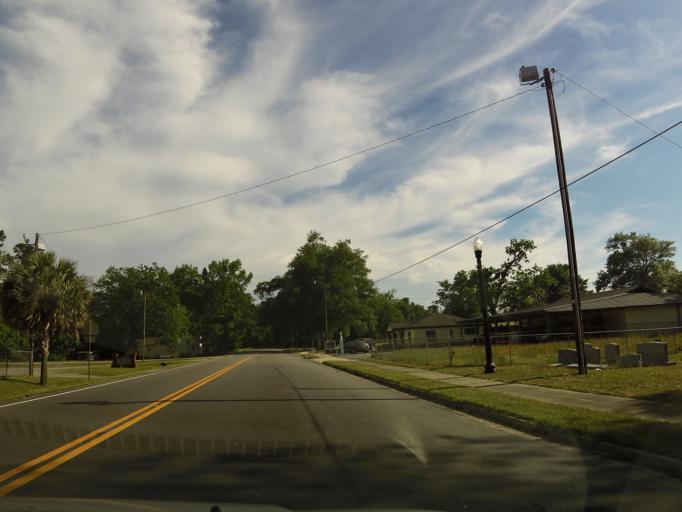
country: US
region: South Carolina
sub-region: Allendale County
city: Fairfax
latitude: 32.9510
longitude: -81.2360
